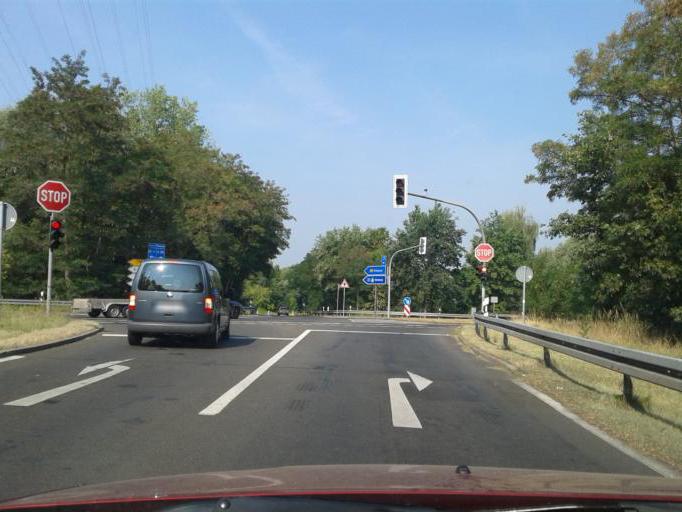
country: DE
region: Brandenburg
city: Birkenwerder
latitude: 52.7006
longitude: 13.2749
